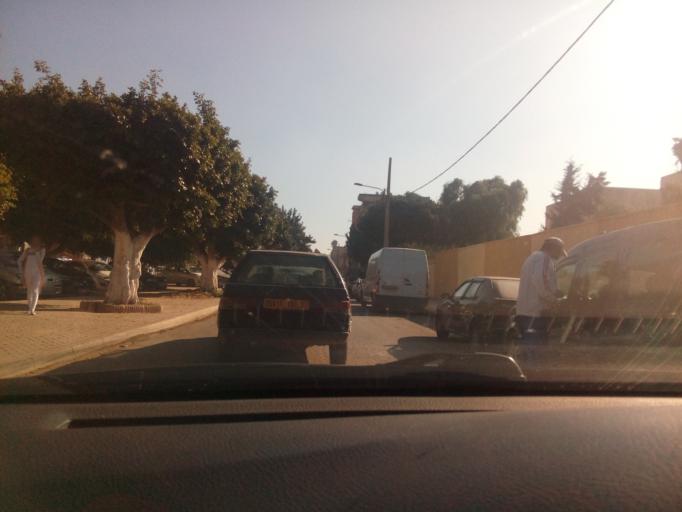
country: DZ
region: Oran
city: Es Senia
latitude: 35.6503
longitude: -0.6264
